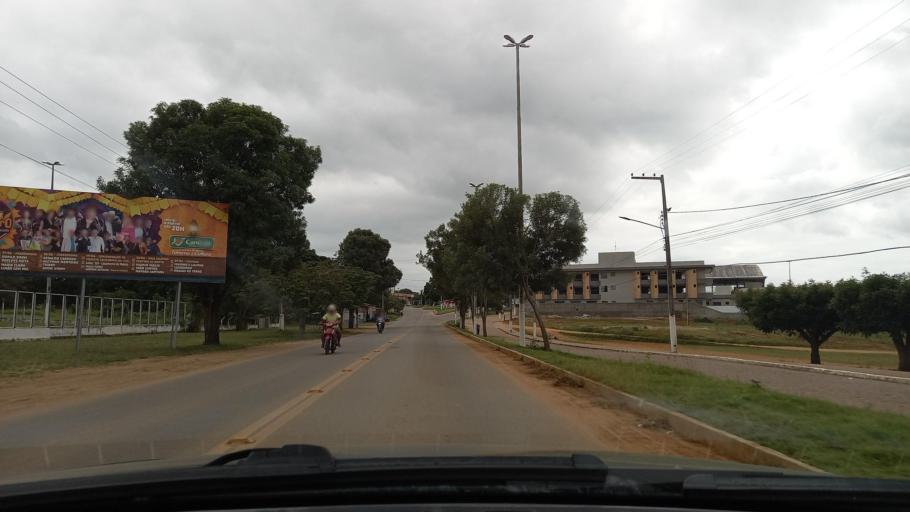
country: BR
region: Sergipe
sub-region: Caninde De Sao Francisco
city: Caninde de Sao Francisco
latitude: -9.6693
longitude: -37.7935
